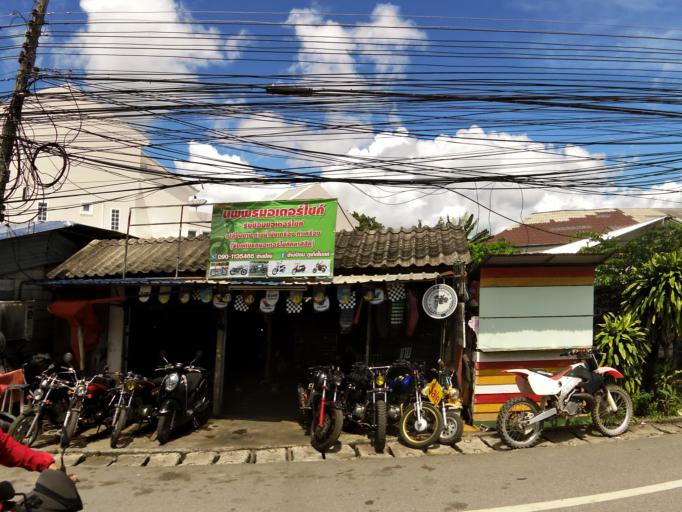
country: TH
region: Phuket
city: Ban Chalong
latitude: 7.8317
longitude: 98.3395
